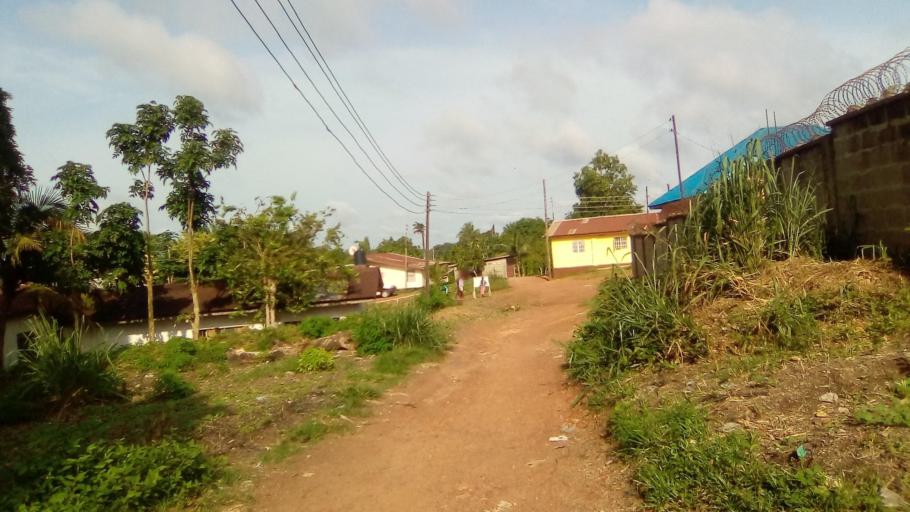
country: SL
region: Southern Province
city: Bo
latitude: 7.9545
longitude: -11.7575
